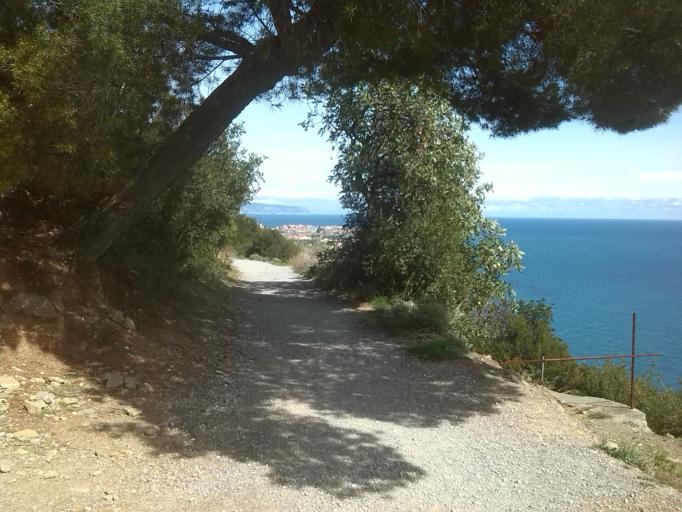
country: IT
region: Liguria
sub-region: Provincia di Savona
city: San Fedele-Lusignano
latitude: 44.0265
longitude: 8.1964
